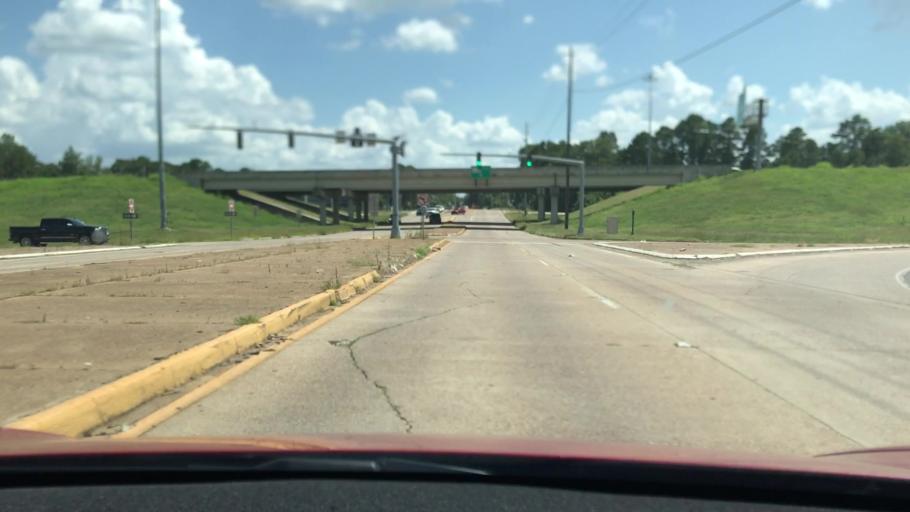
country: US
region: Louisiana
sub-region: Bossier Parish
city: Bossier City
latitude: 32.4172
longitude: -93.7371
